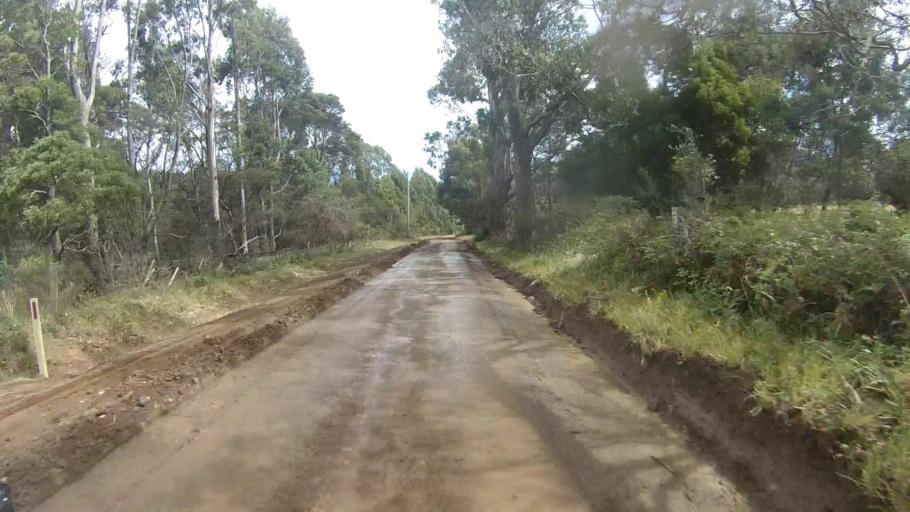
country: AU
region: Tasmania
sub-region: Sorell
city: Sorell
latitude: -42.7730
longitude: 147.8087
